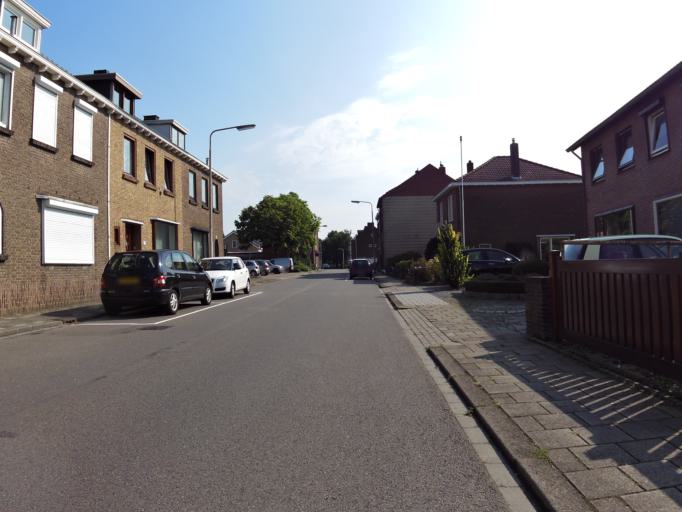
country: NL
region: Limburg
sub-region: Gemeente Kerkrade
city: Kerkrade
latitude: 50.8644
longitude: 6.0413
